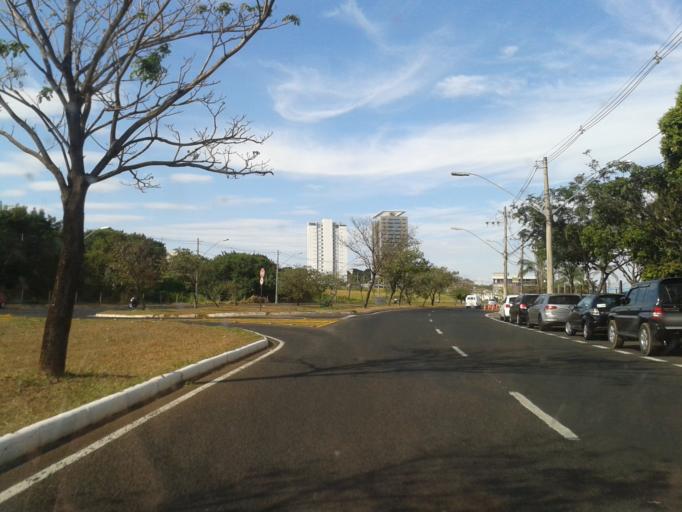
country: BR
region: Minas Gerais
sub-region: Uberlandia
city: Uberlandia
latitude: -18.9110
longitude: -48.2551
